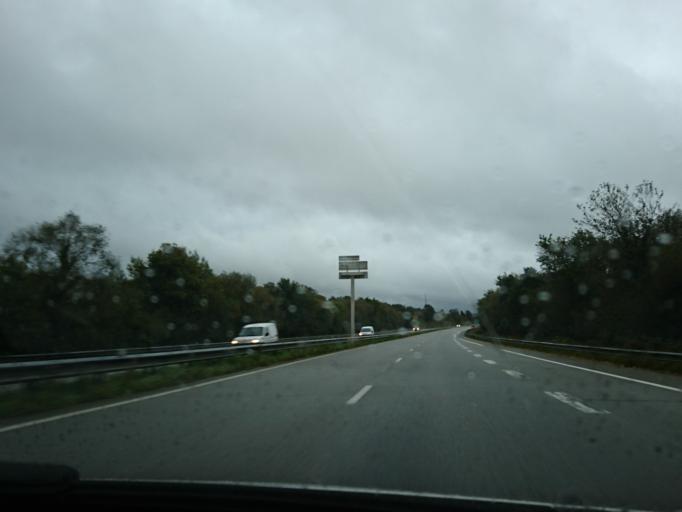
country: FR
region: Brittany
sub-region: Departement du Finistere
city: Chateaulin
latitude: 48.2115
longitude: -4.0482
